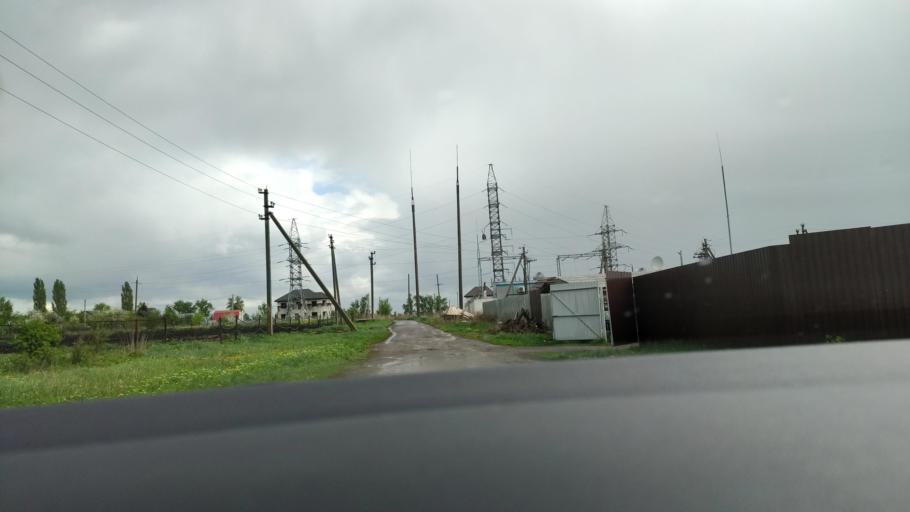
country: RU
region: Voronezj
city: Maslovka
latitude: 51.5022
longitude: 39.3032
